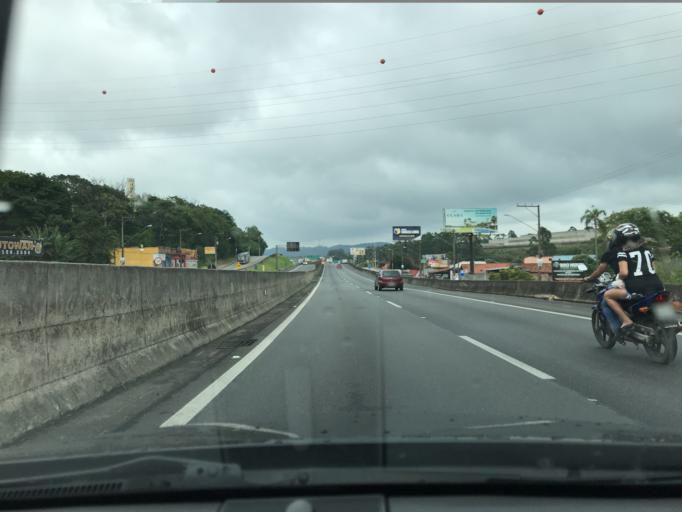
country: BR
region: Sao Paulo
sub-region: Vargem Grande Paulista
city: Vargem Grande Paulista
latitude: -23.6093
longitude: -47.0083
